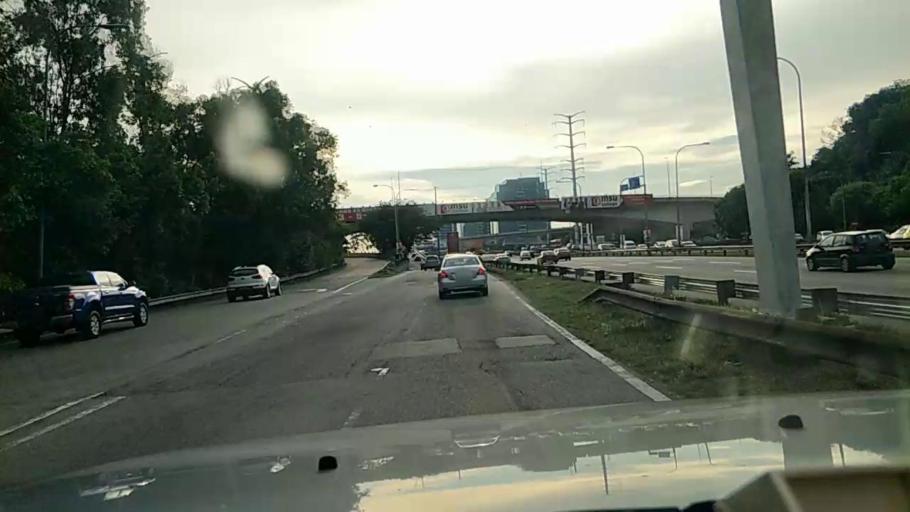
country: MY
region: Selangor
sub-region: Petaling
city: Petaling Jaya
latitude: 3.0841
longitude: 101.5951
